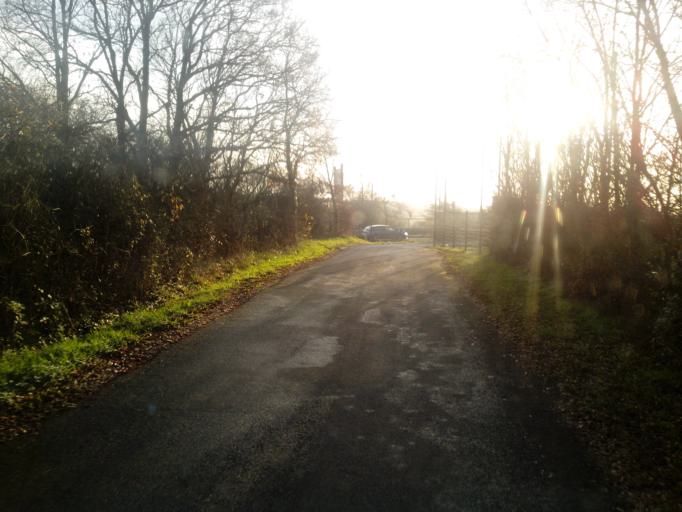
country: FR
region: Pays de la Loire
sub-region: Departement de Maine-et-Loire
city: Cholet
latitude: 47.0596
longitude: -0.9072
